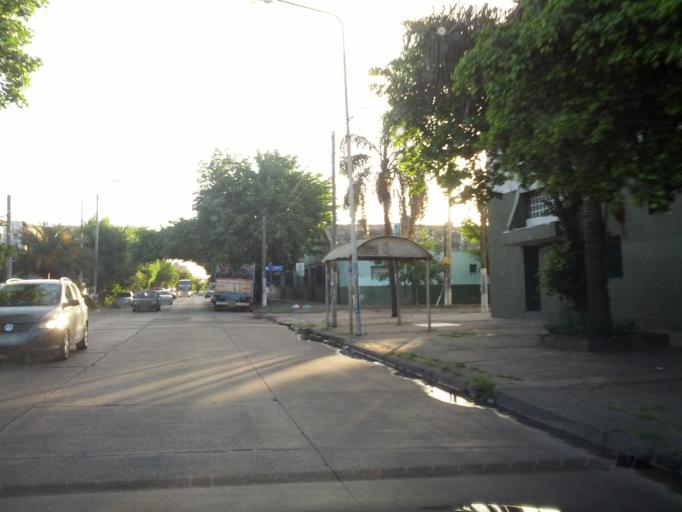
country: AR
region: Buenos Aires
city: San Justo
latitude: -34.6501
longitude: -58.5313
